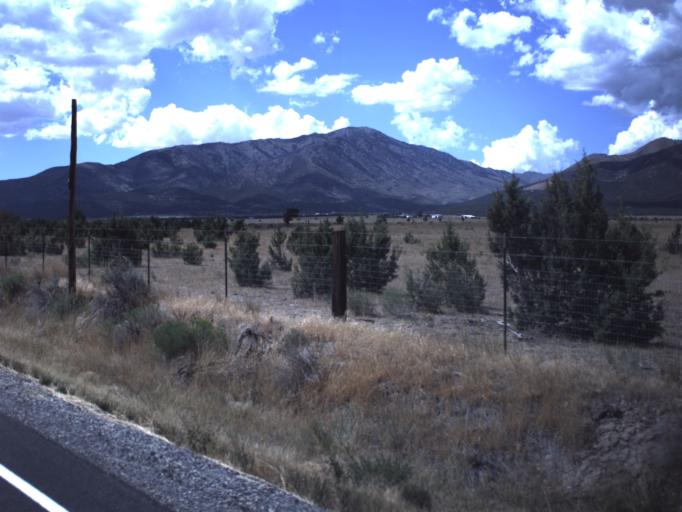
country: US
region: Utah
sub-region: Tooele County
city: Grantsville
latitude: 40.3362
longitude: -112.4964
